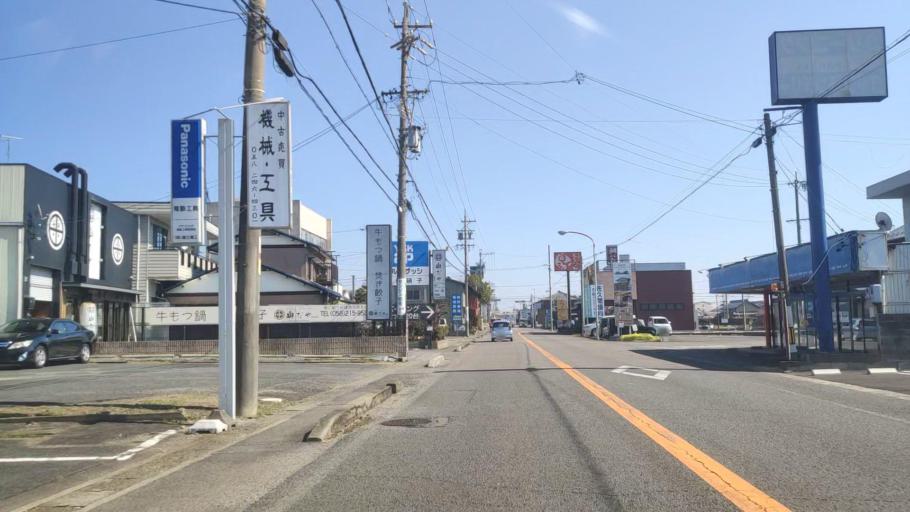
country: JP
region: Gifu
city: Kasamatsucho
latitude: 35.3925
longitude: 136.7919
